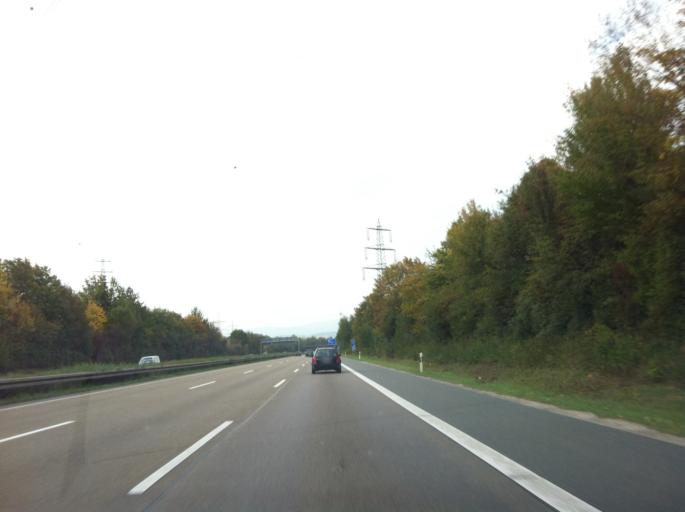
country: DE
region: Hesse
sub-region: Regierungsbezirk Darmstadt
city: Hattersheim
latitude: 50.0796
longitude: 8.4839
